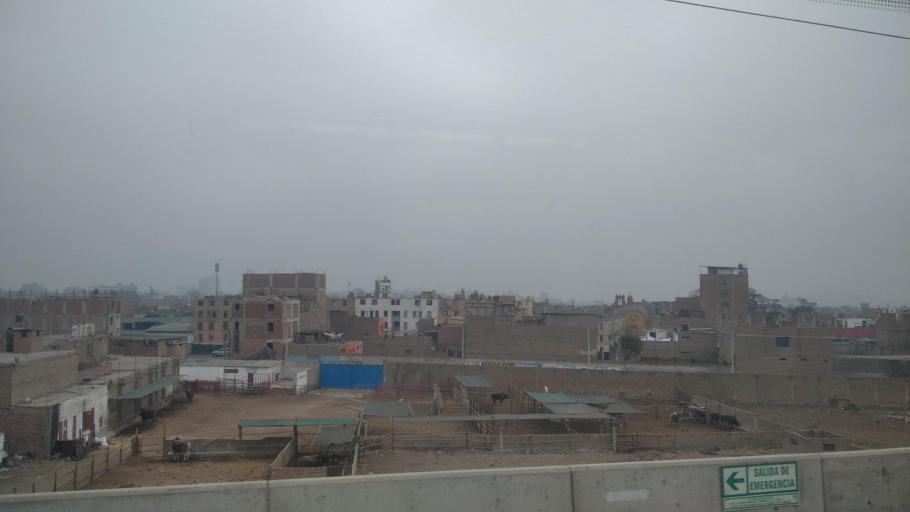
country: PE
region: Lima
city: Lima
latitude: -12.0453
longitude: -77.0100
